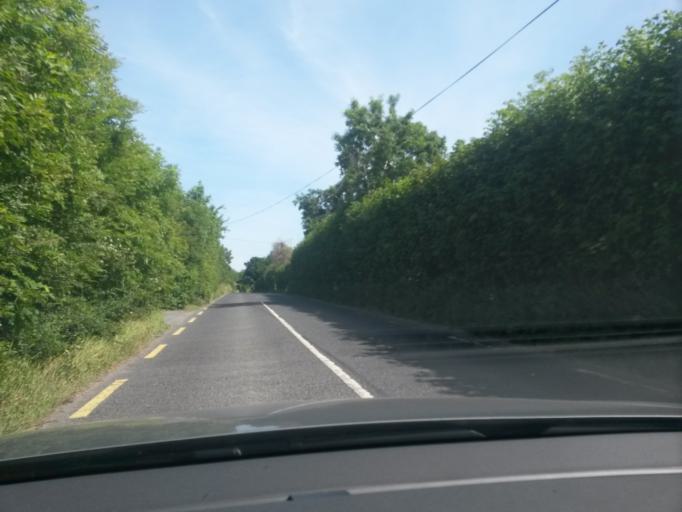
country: IE
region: Leinster
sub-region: Kildare
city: Eadestown
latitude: 53.1958
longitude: -6.5668
